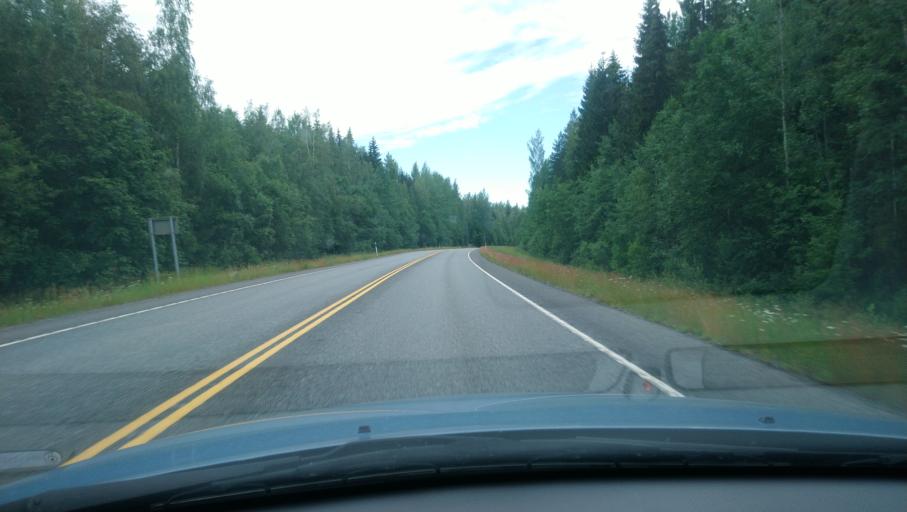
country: FI
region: Uusimaa
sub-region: Porvoo
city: Porvoo
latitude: 60.4355
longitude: 25.5748
